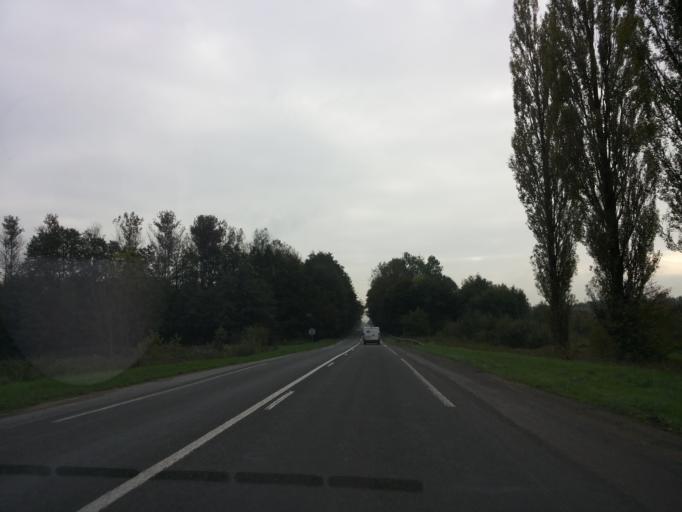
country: FR
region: Champagne-Ardenne
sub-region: Departement des Ardennes
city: Bazeilles
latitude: 49.6773
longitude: 5.0061
